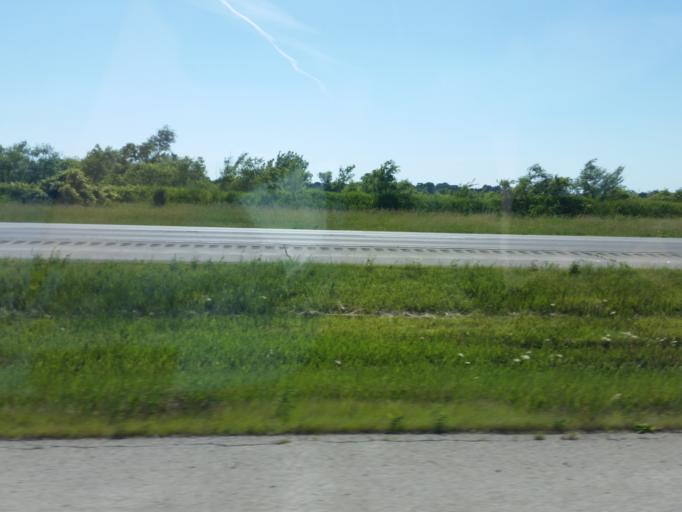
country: US
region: Illinois
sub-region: Winnebago County
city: Roscoe
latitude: 42.4382
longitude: -89.0170
